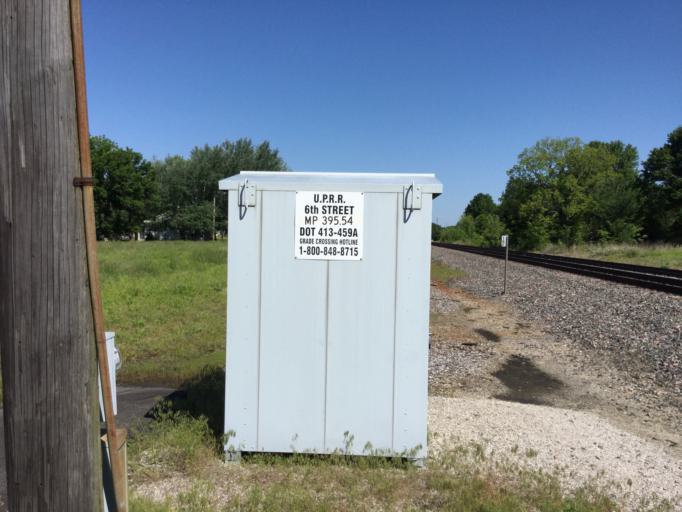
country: US
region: Kansas
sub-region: Labette County
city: Oswego
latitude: 37.2303
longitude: -95.1834
